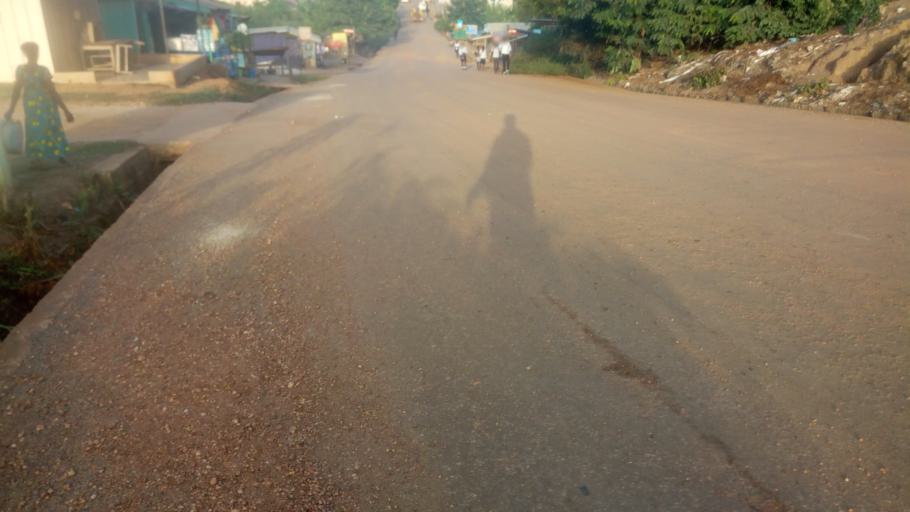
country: GH
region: Ashanti
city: Obuasi
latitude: 6.2132
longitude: -1.6978
